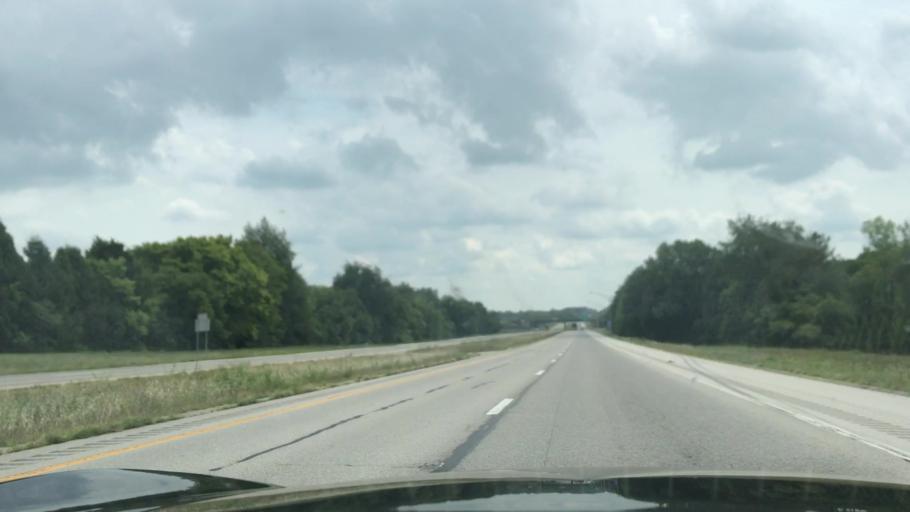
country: US
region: Kentucky
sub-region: Warren County
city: Bowling Green
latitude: 36.9980
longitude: -86.5056
